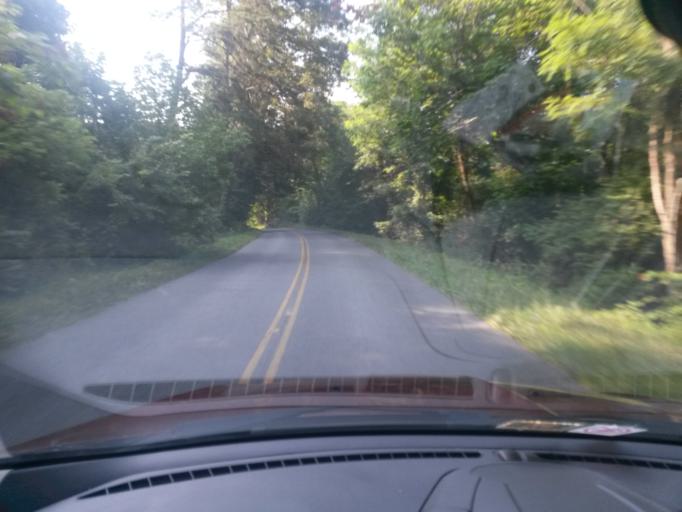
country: US
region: Virginia
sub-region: Giles County
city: Narrows
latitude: 37.3936
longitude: -80.7939
